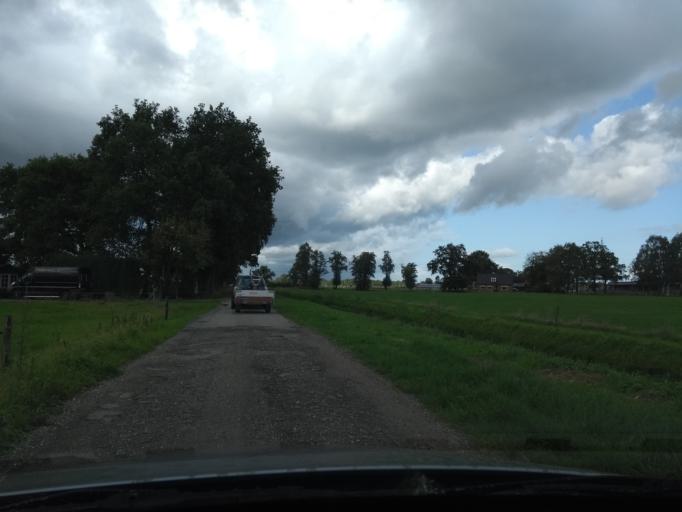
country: NL
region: Overijssel
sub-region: Gemeente Raalte
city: Raalte
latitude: 52.3669
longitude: 6.3366
